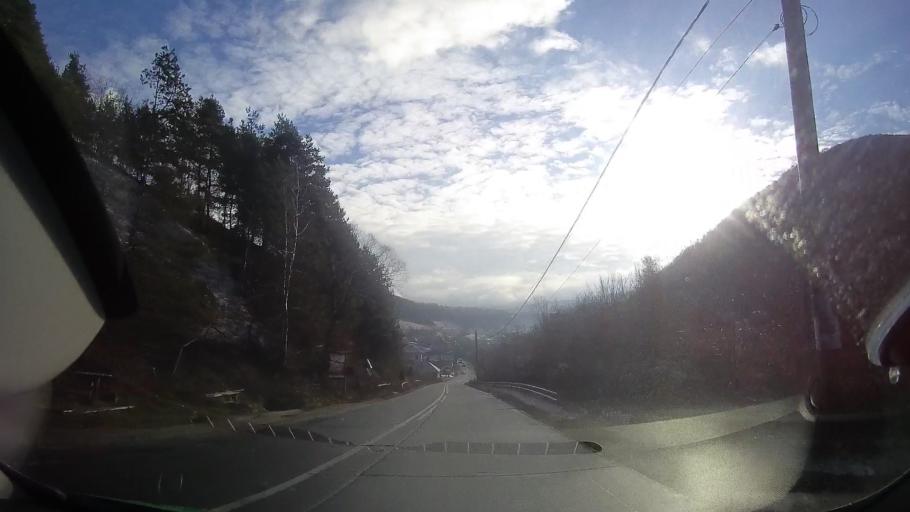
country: RO
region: Alba
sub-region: Comuna Sohodol
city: Sohodol
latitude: 46.3731
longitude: 23.0193
